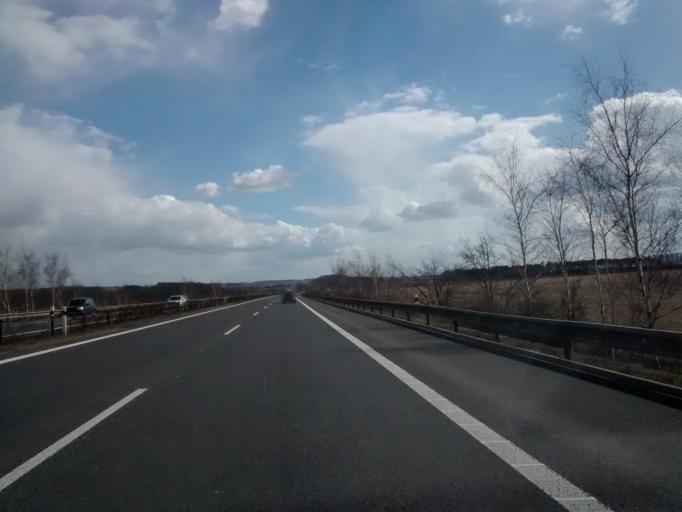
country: CZ
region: Ustecky
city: Roudnice nad Labem
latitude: 50.3874
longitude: 14.2370
